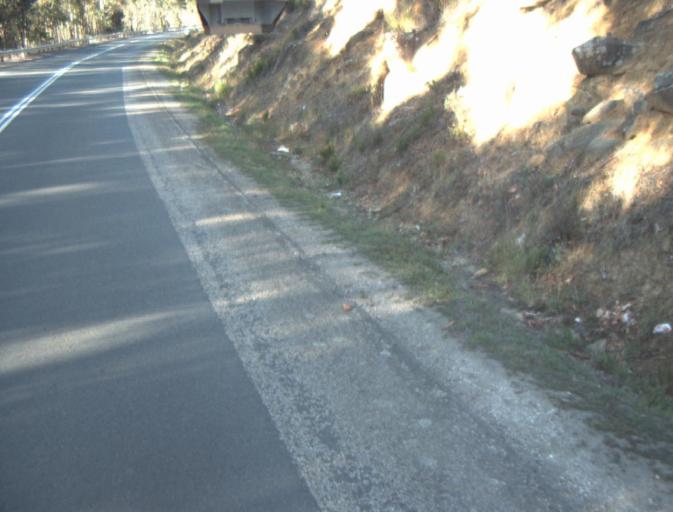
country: AU
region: Tasmania
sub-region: Launceston
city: Mayfield
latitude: -41.3236
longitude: 147.1872
